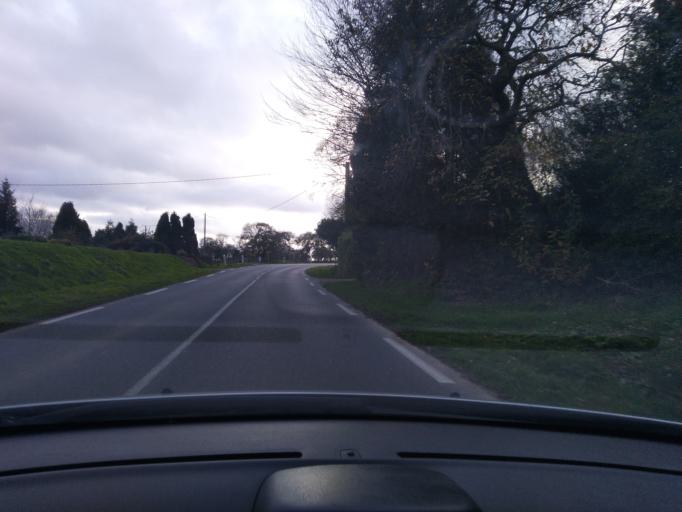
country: FR
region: Brittany
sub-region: Departement des Cotes-d'Armor
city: Plouaret
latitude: 48.6034
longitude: -3.4863
